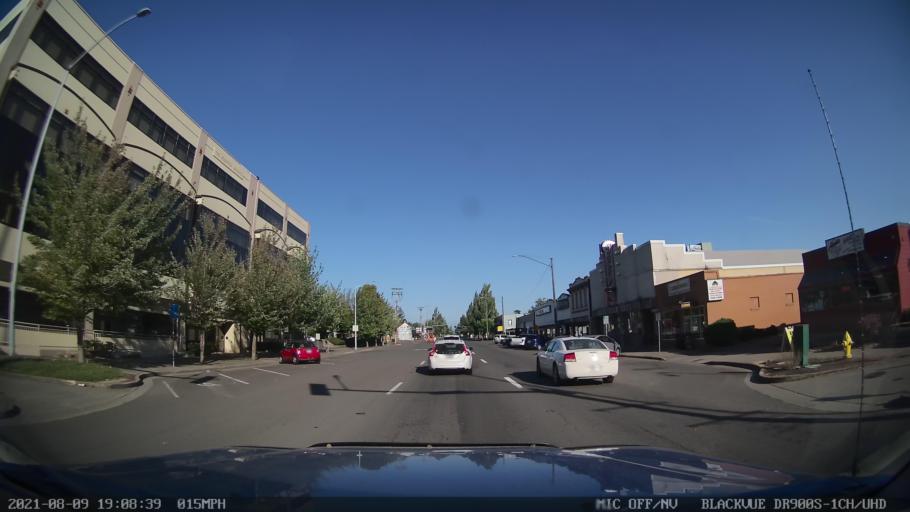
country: US
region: Oregon
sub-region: Marion County
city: Salem
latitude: 44.9369
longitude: -123.0270
